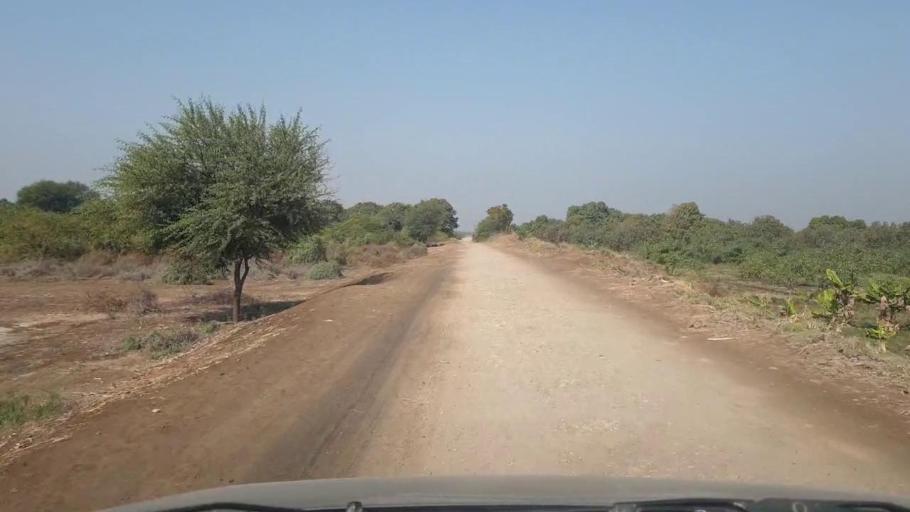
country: PK
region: Sindh
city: Mirwah Gorchani
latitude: 25.2494
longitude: 69.1060
